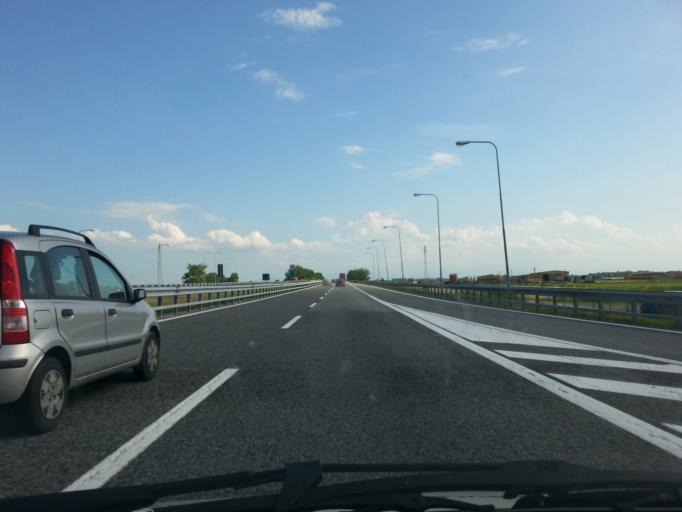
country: IT
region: Piedmont
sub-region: Provincia di Cuneo
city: Marene
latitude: 44.7031
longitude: 7.7633
